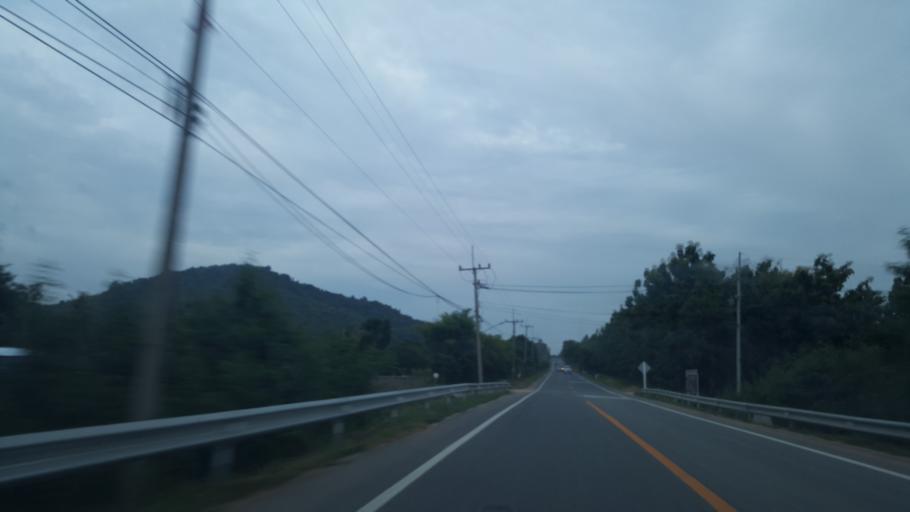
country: TH
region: Chon Buri
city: Ban Talat Bueng
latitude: 12.9752
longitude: 101.0049
